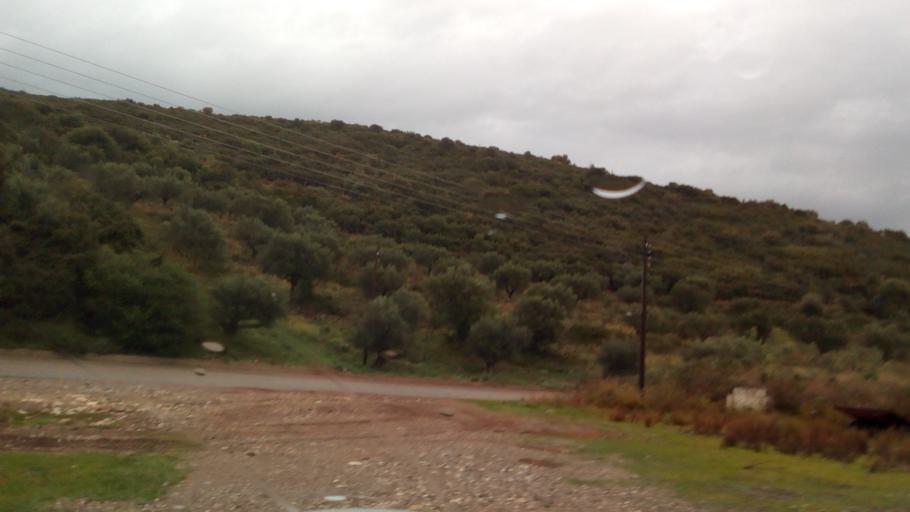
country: GR
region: West Greece
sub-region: Nomos Aitolias kai Akarnanias
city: Nafpaktos
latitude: 38.4165
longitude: 21.9037
